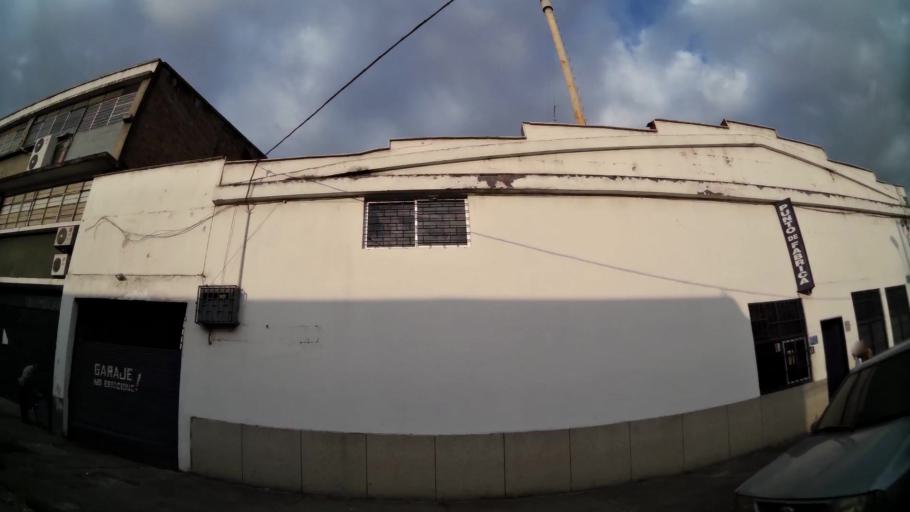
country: CO
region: Valle del Cauca
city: Cali
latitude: 3.4539
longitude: -76.5203
